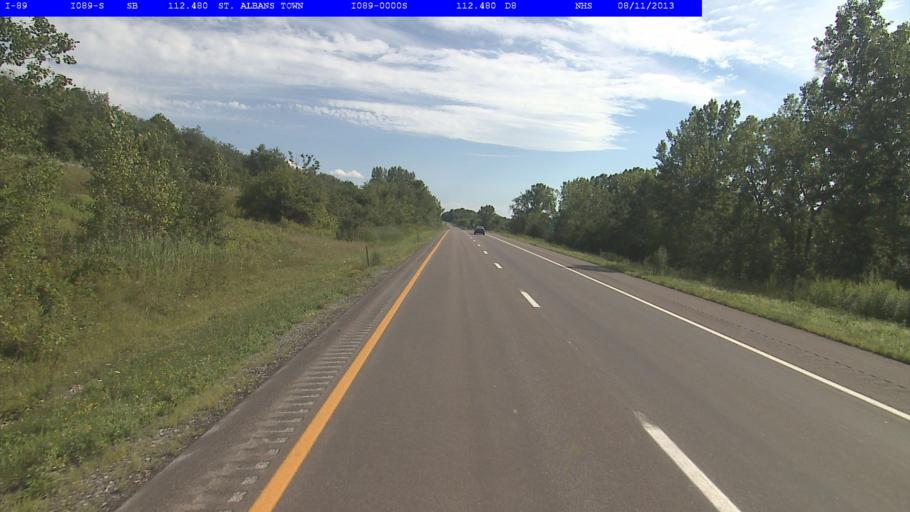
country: US
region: Vermont
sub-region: Franklin County
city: Saint Albans
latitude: 44.7770
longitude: -73.0746
